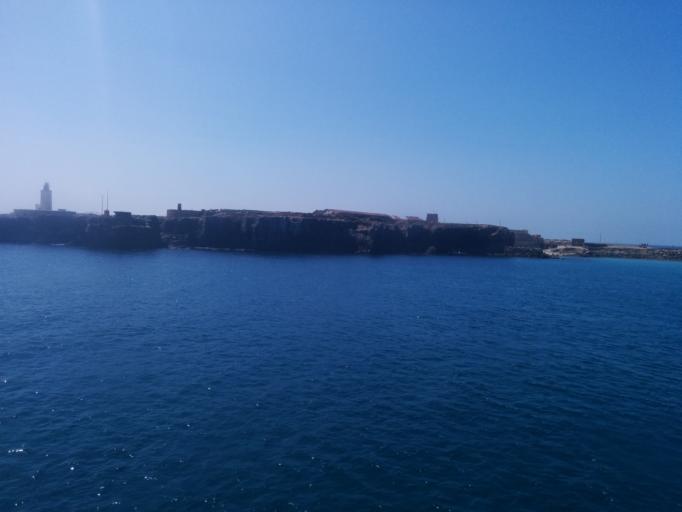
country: ES
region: Andalusia
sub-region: Provincia de Cadiz
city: Tarifa
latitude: 36.0054
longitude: -5.6046
